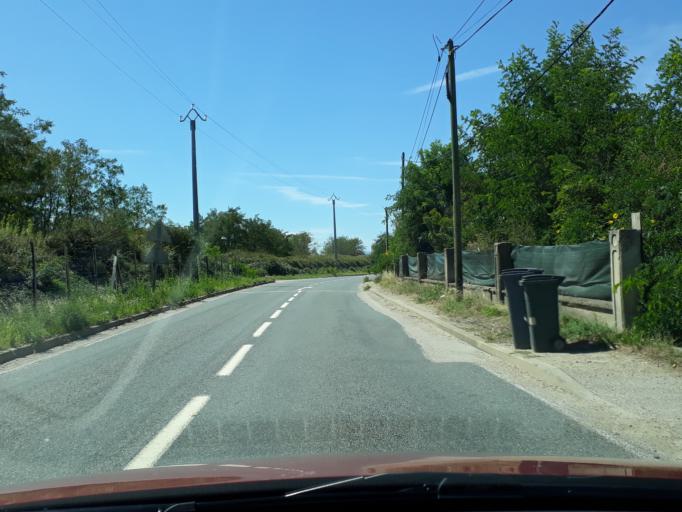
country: FR
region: Rhone-Alpes
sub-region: Departement du Rhone
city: Saint-Bonnet-de-Mure
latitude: 45.6732
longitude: 5.0178
